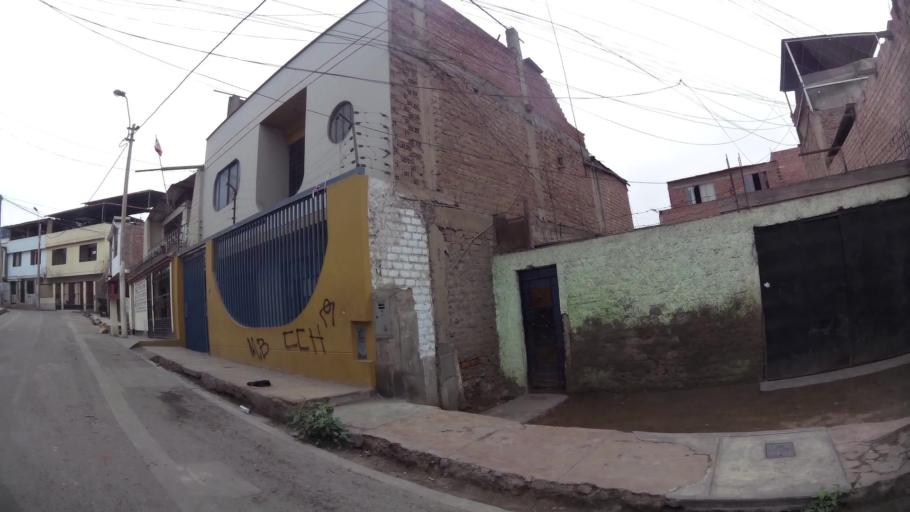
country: PE
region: Lima
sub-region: Lima
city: Surco
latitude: -12.1784
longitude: -76.9483
